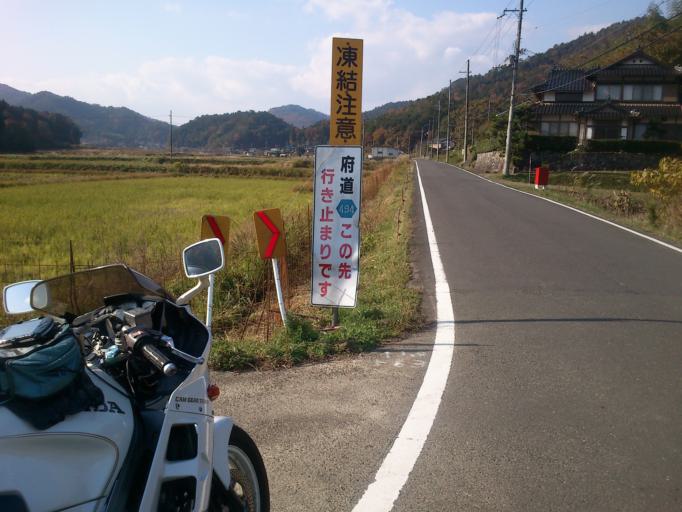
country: JP
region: Kyoto
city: Ayabe
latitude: 35.3756
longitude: 135.2355
